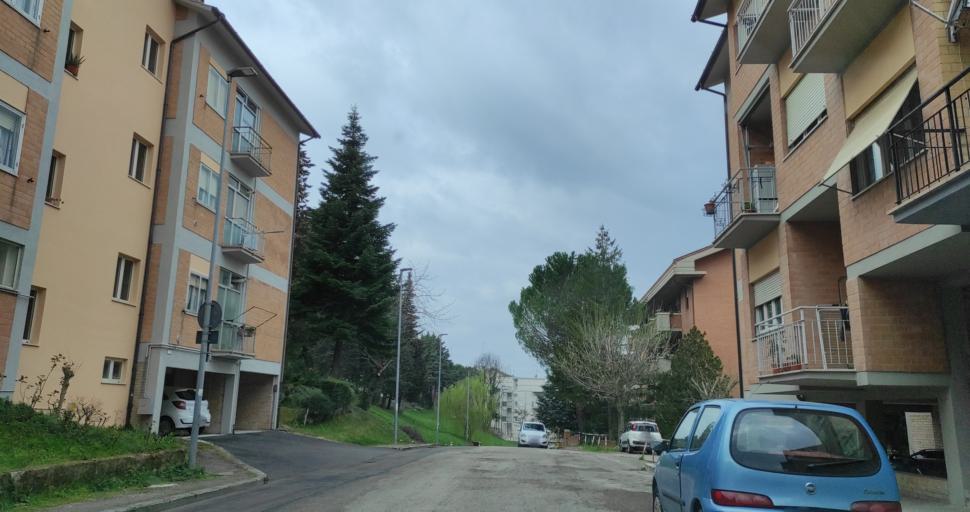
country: IT
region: The Marches
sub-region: Provincia di Macerata
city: Sforzacosta
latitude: 43.2826
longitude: 13.4297
